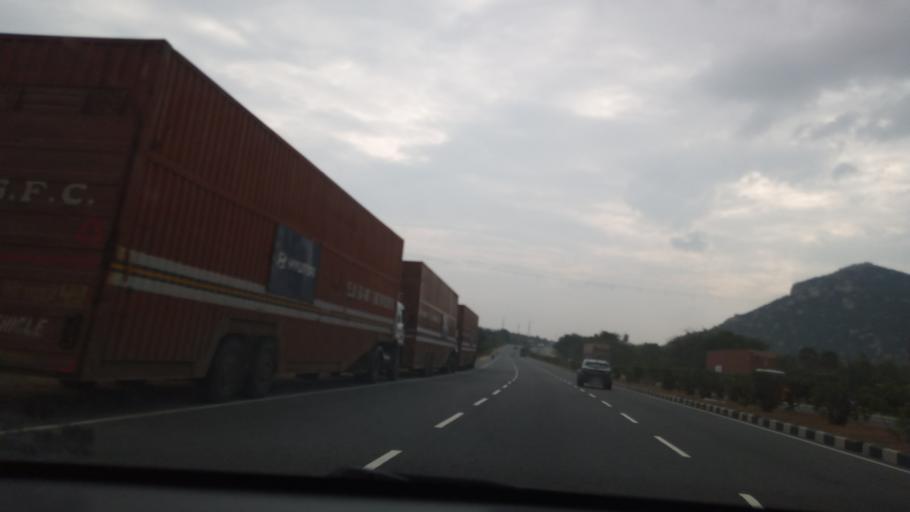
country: IN
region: Tamil Nadu
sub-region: Vellore
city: Jolarpettai
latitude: 12.5635
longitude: 78.4670
